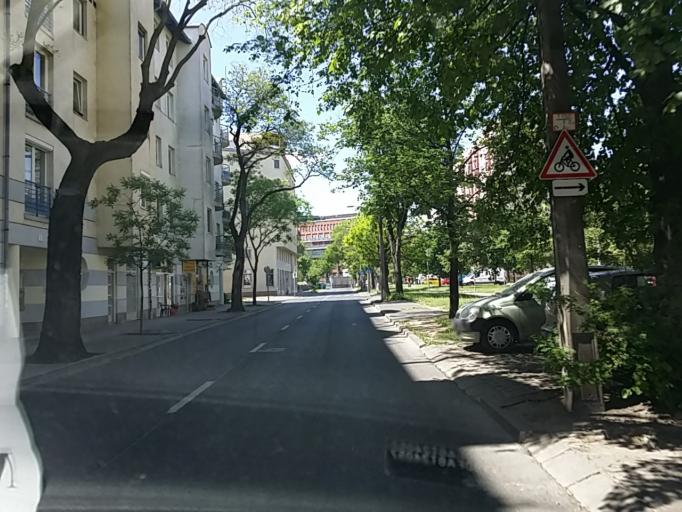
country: HU
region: Budapest
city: Budapest XIII. keruelet
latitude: 47.5309
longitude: 19.0768
